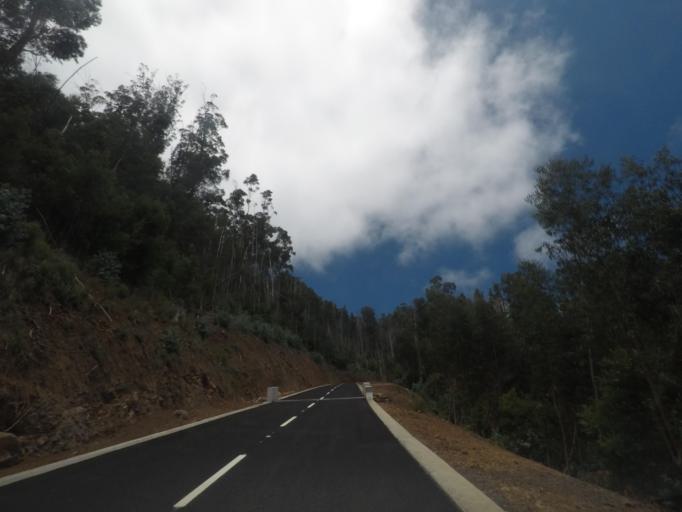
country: PT
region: Madeira
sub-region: Calheta
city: Estreito da Calheta
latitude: 32.7459
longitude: -17.1580
